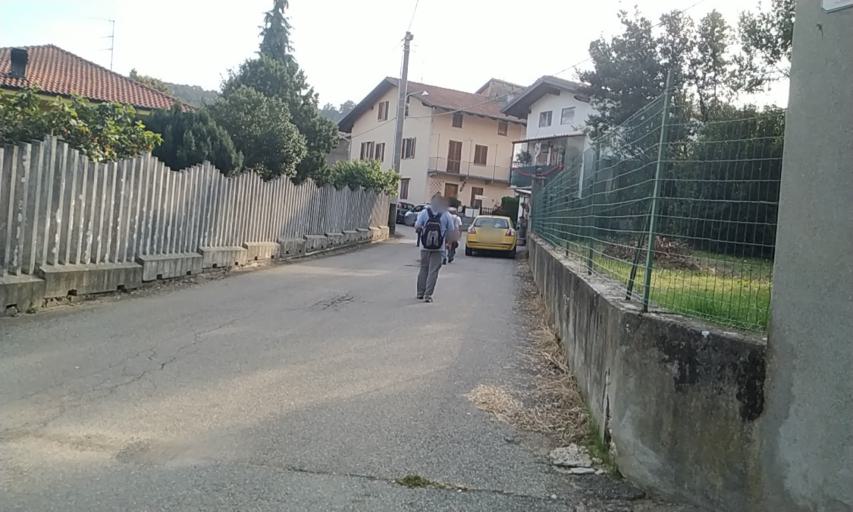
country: IT
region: Piedmont
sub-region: Provincia di Biella
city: Dorzano
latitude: 45.4373
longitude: 8.0918
